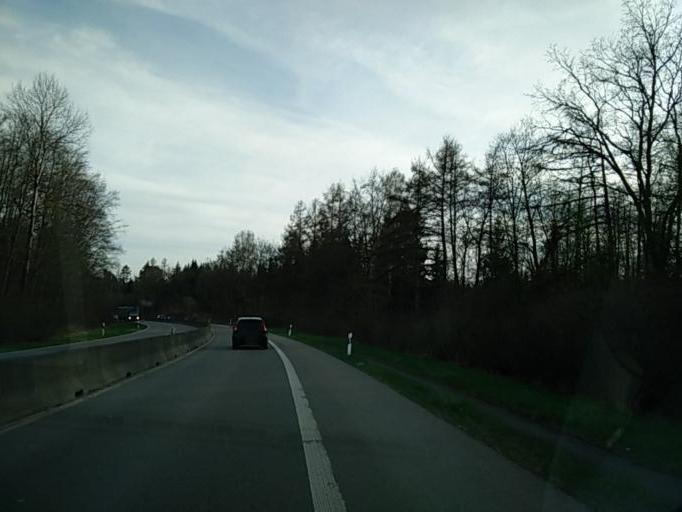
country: DE
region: Baden-Wuerttemberg
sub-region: Regierungsbezirk Stuttgart
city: Weil im Schonbuch
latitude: 48.5902
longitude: 9.0628
